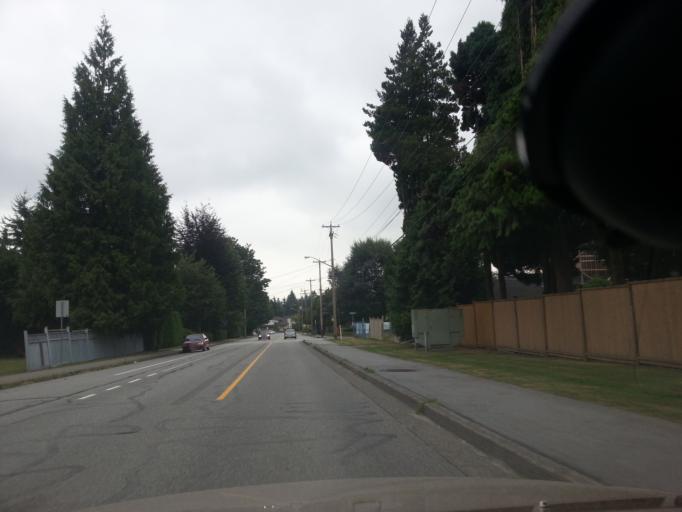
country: CA
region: British Columbia
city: Port Moody
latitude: 49.2726
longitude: -122.8806
